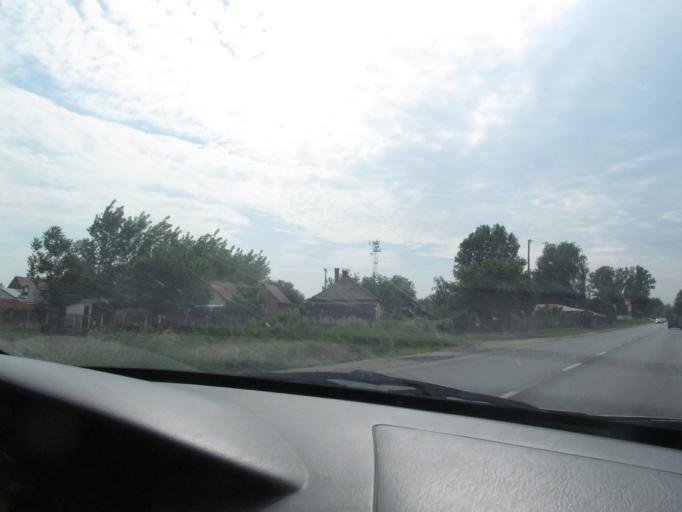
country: HU
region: Szabolcs-Szatmar-Bereg
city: Nyirtelek
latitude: 48.0077
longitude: 21.6358
